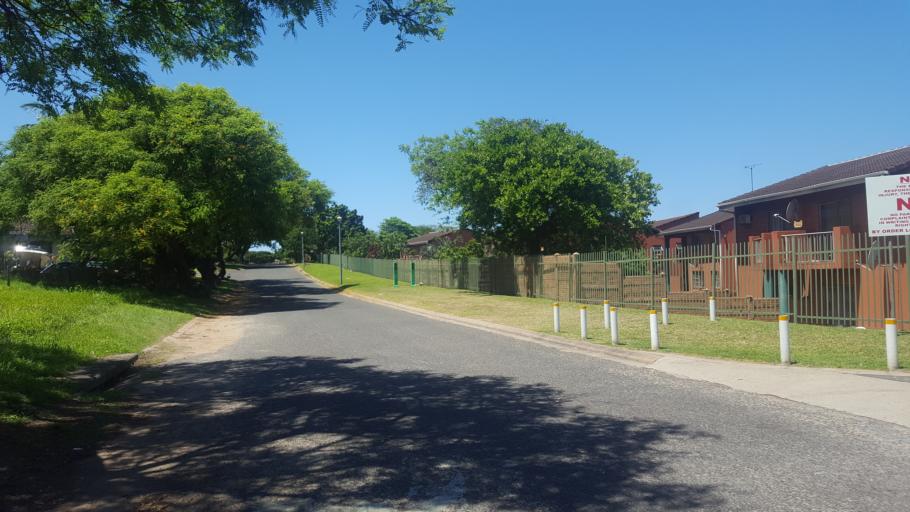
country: ZA
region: KwaZulu-Natal
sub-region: uThungulu District Municipality
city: Richards Bay
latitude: -28.7661
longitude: 32.0667
